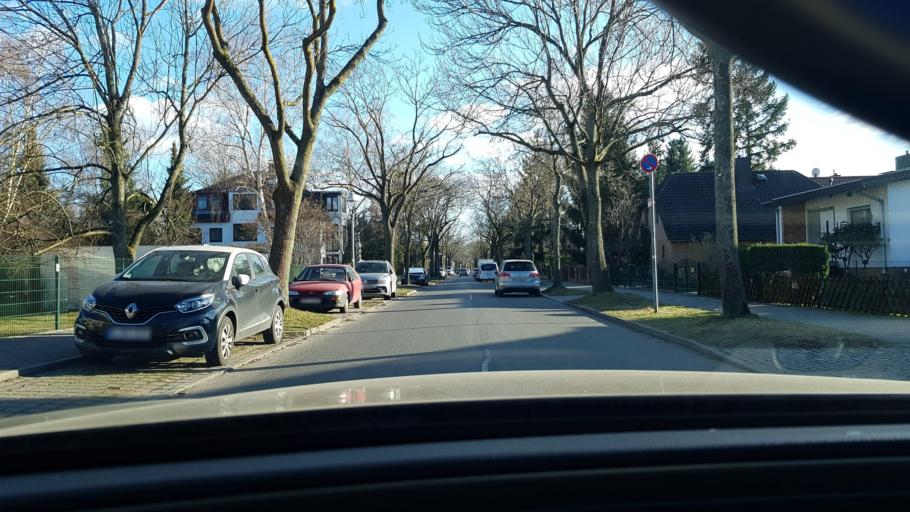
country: DE
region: Berlin
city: Rudow
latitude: 52.4093
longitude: 13.4990
